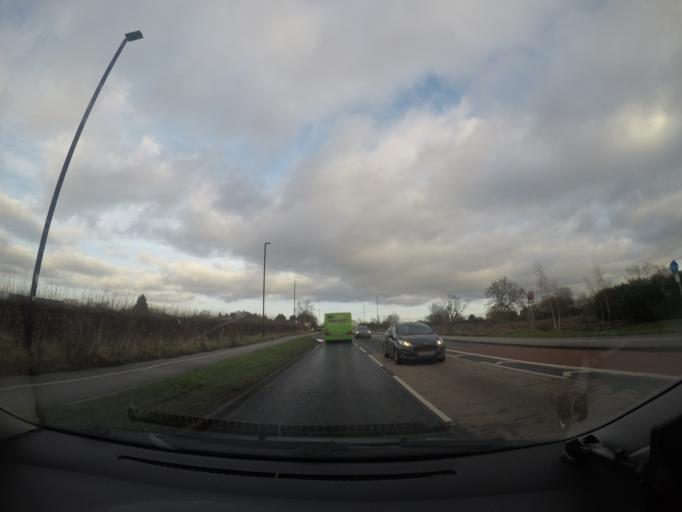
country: GB
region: England
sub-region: City of York
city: Huntington
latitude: 53.9777
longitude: -1.0531
